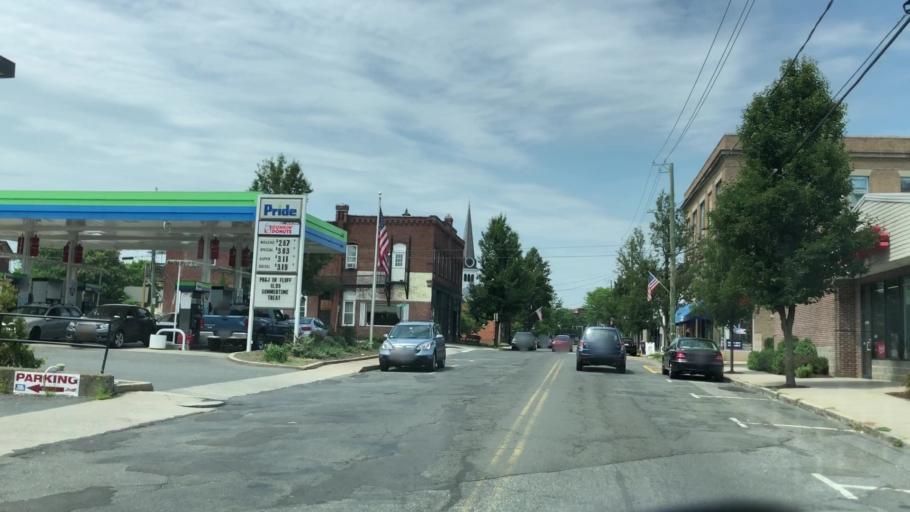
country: US
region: Massachusetts
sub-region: Hampshire County
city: Easthampton
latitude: 42.2681
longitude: -72.6708
